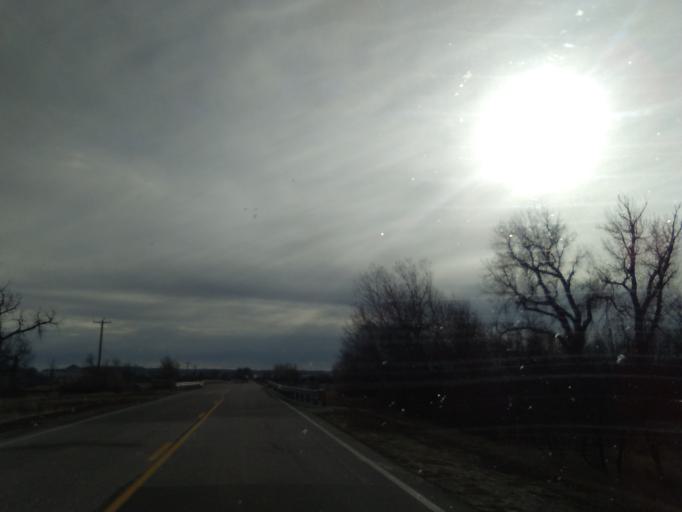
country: US
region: Nebraska
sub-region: Scotts Bluff County
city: Gering
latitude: 41.7909
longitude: -103.5191
